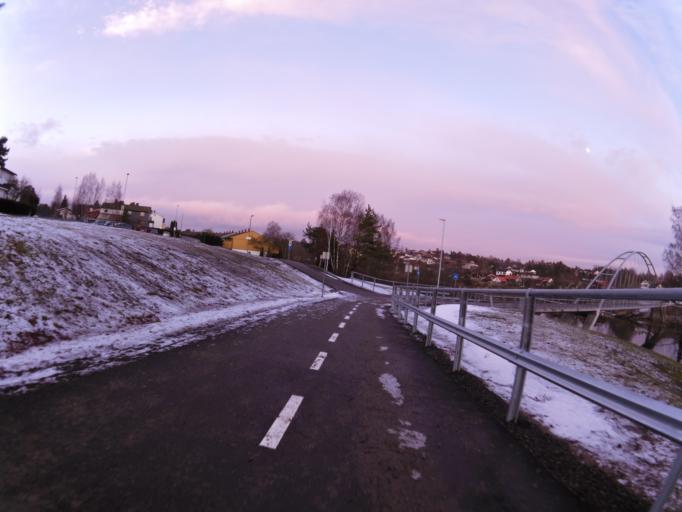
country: NO
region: Ostfold
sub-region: Sarpsborg
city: Sarpsborg
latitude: 59.2909
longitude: 11.1353
